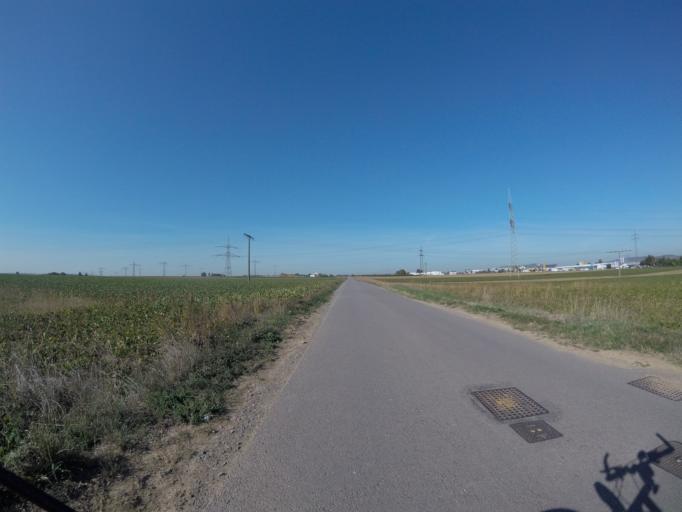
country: DE
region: Baden-Wuerttemberg
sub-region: Regierungsbezirk Stuttgart
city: Bietigheim-Bissingen
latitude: 48.9543
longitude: 9.0885
